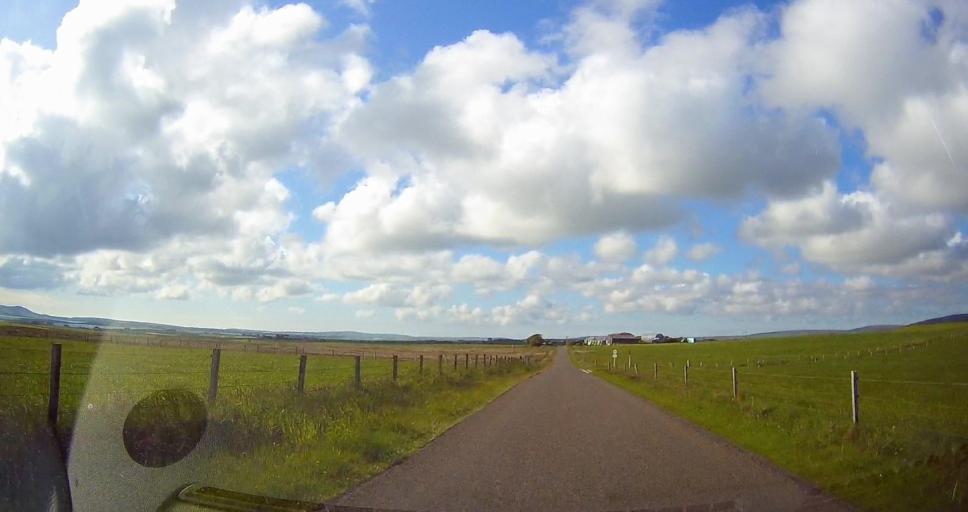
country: GB
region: Scotland
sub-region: Orkney Islands
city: Stromness
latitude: 58.9899
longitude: -3.1550
